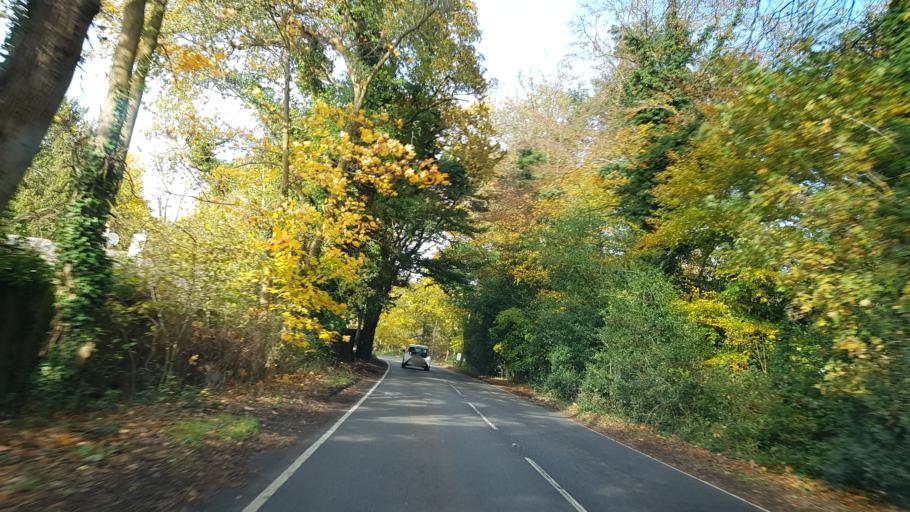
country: GB
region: England
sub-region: Surrey
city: Seale
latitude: 51.1983
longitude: -0.7447
